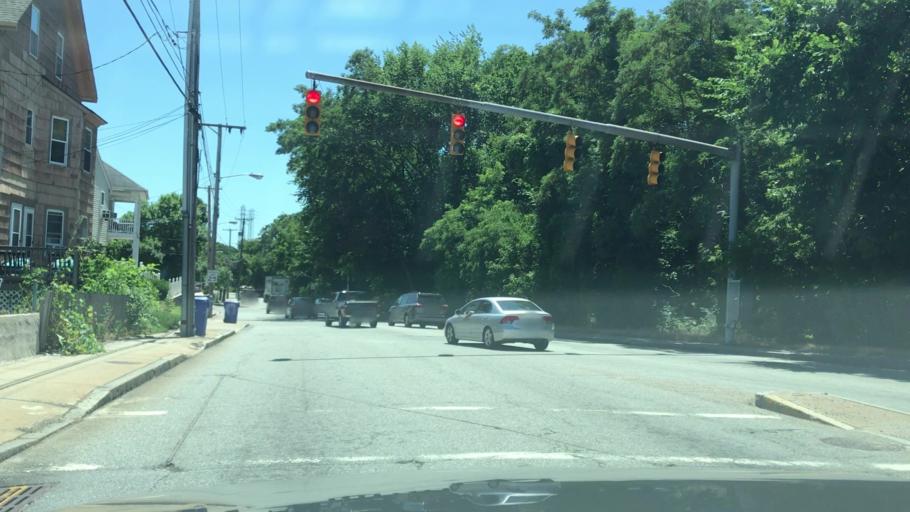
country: US
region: Rhode Island
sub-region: Providence County
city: Pawtucket
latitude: 41.8715
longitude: -71.3804
